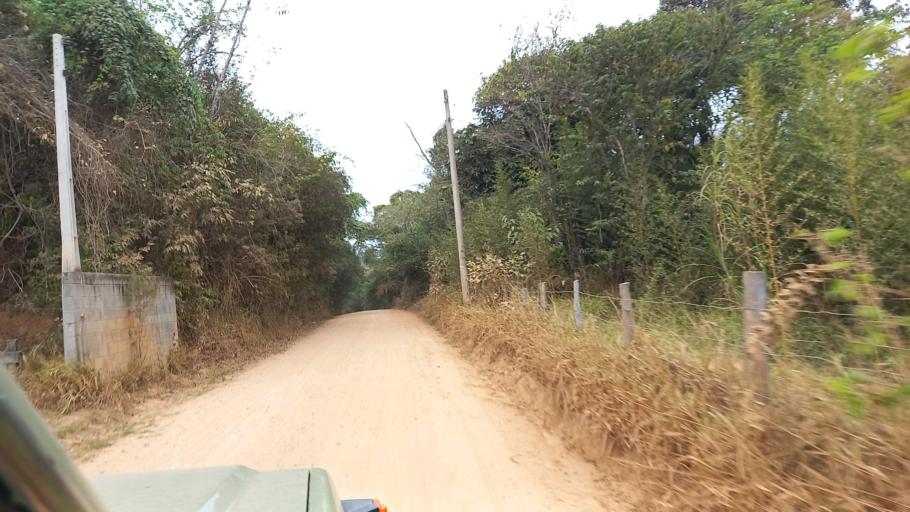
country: BR
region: Sao Paulo
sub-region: Moji-Guacu
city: Mogi-Gaucu
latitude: -22.2977
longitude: -46.8329
